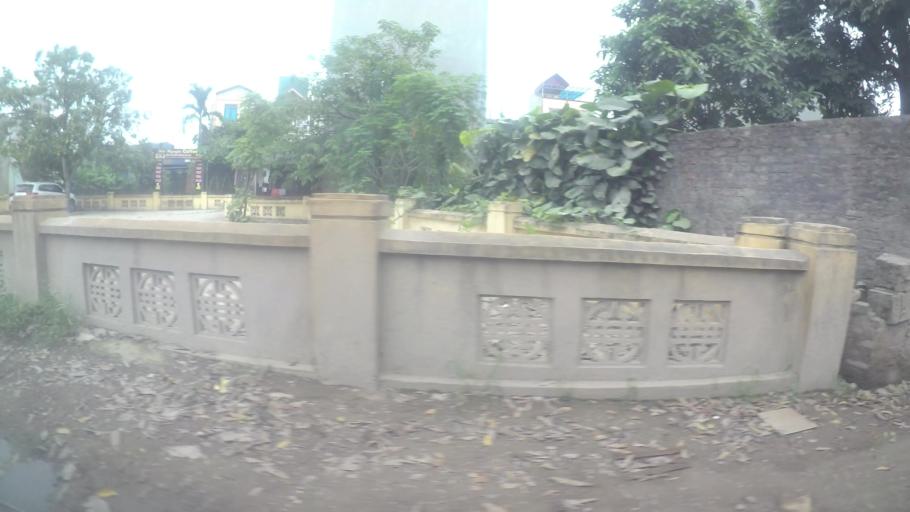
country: VN
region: Ha Noi
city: Cau Dien
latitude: 21.0393
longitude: 105.7380
